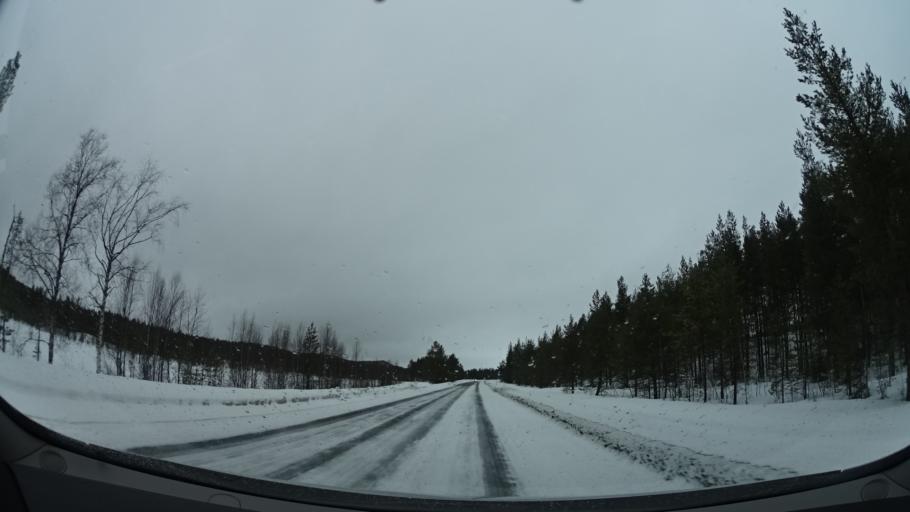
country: SE
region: Vaesterbotten
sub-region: Mala Kommun
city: Mala
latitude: 65.1552
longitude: 18.7956
